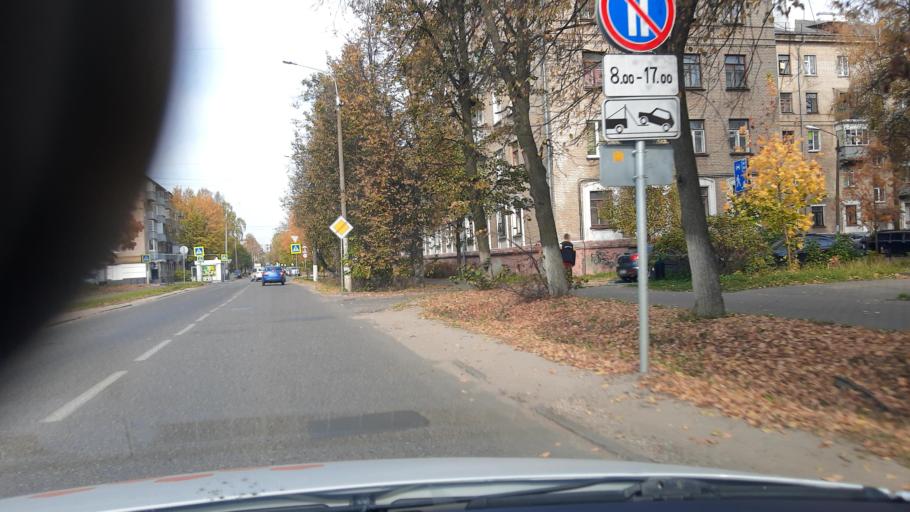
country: RU
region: Moskovskaya
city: Elektrostal'
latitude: 55.7966
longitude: 38.4361
